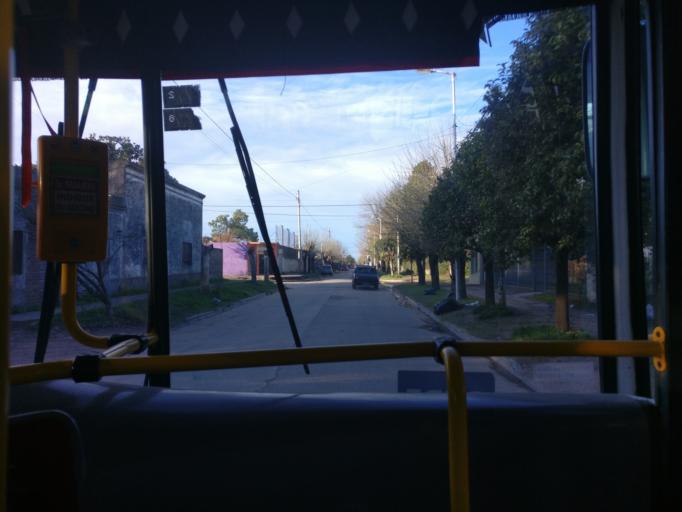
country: AR
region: Buenos Aires
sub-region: Partido de Ezeiza
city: Ezeiza
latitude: -34.9421
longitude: -58.6148
